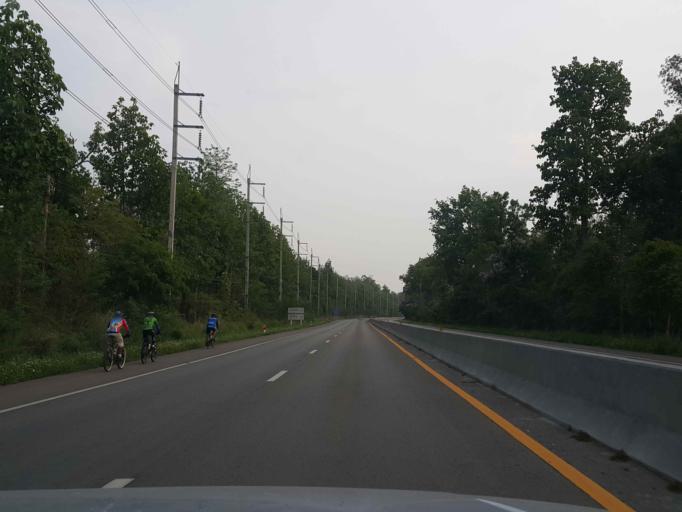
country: TH
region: Chiang Mai
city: Mae Taeng
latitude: 19.1605
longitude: 98.9482
